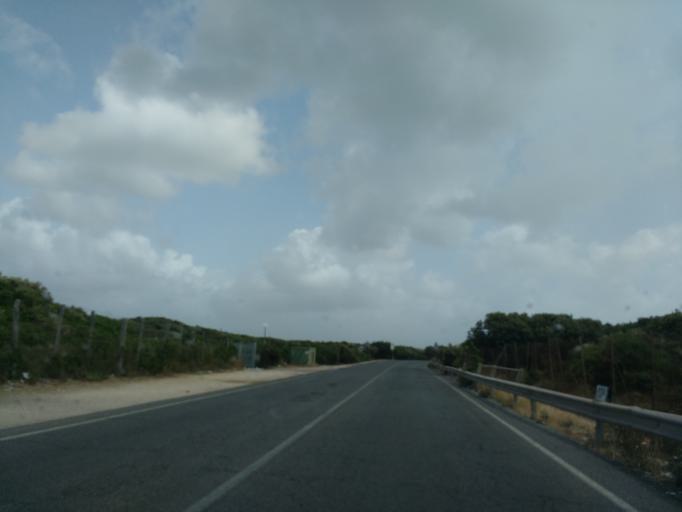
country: IT
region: Latium
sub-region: Citta metropolitana di Roma Capitale
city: Torvaianica
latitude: 41.6711
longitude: 12.3973
